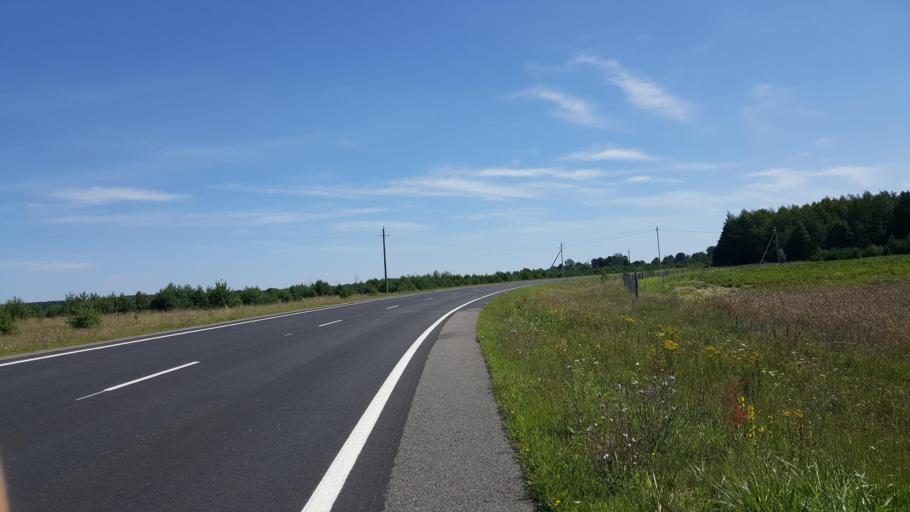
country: BY
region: Brest
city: Kamyanyets
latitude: 52.4005
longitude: 23.9956
